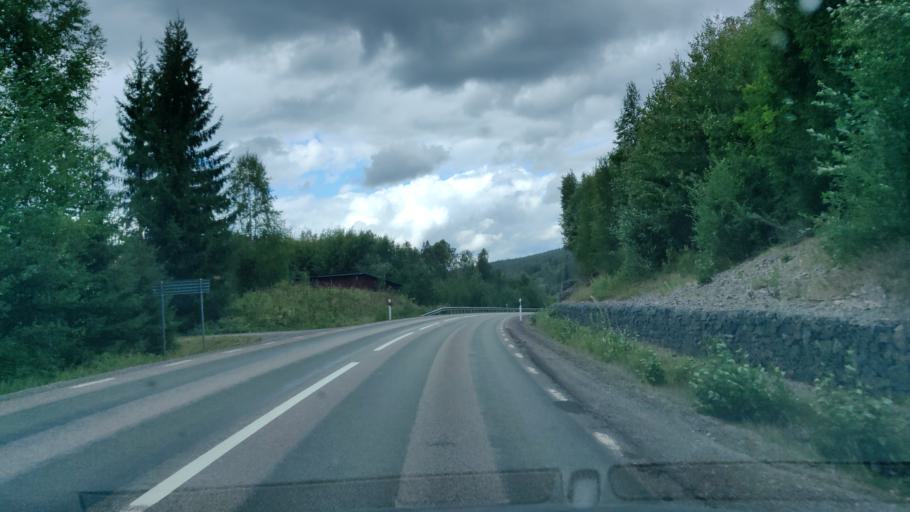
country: SE
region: Vaermland
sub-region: Torsby Kommun
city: Torsby
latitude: 60.5414
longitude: 13.1179
